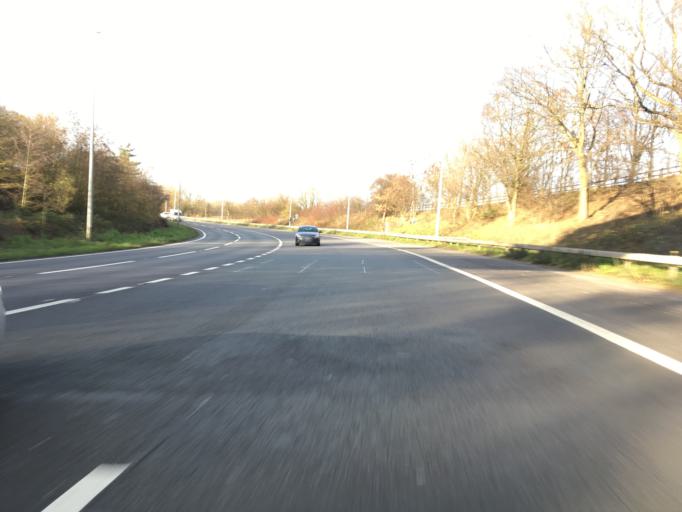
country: GB
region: England
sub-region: Warrington
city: Lymm
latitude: 53.3560
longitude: -2.4994
